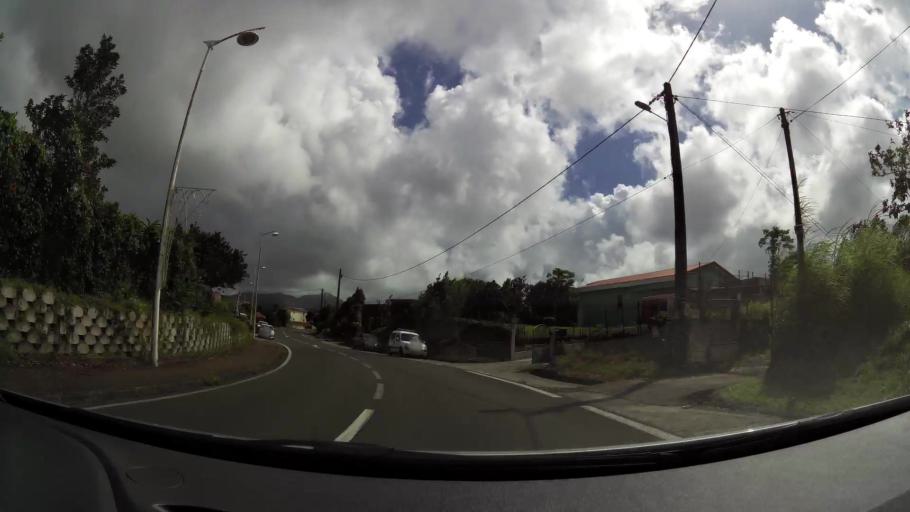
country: MQ
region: Martinique
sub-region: Martinique
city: Le Morne-Rouge
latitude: 14.7860
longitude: -61.1386
